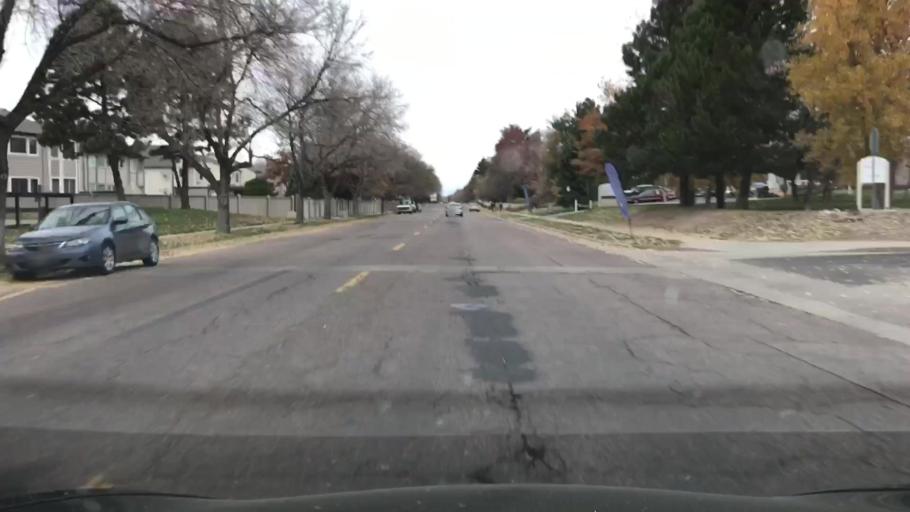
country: US
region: Colorado
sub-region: Arapahoe County
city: Glendale
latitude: 39.6859
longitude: -104.8936
